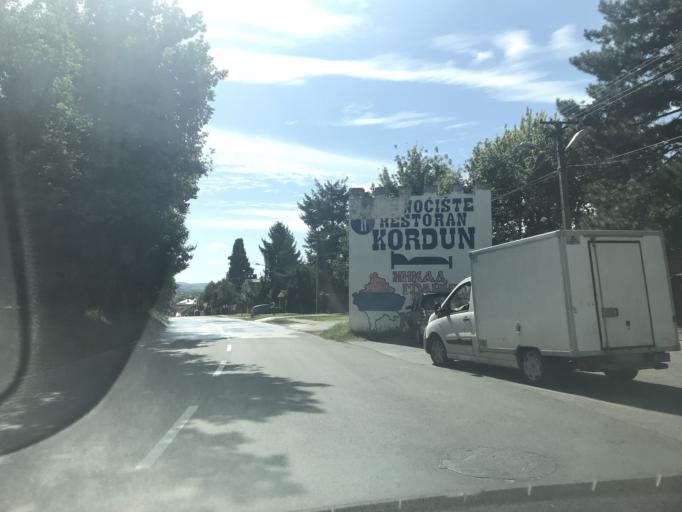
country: RS
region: Autonomna Pokrajina Vojvodina
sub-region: Juznobacki Okrug
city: Novi Sad
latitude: 45.2223
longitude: 19.8513
